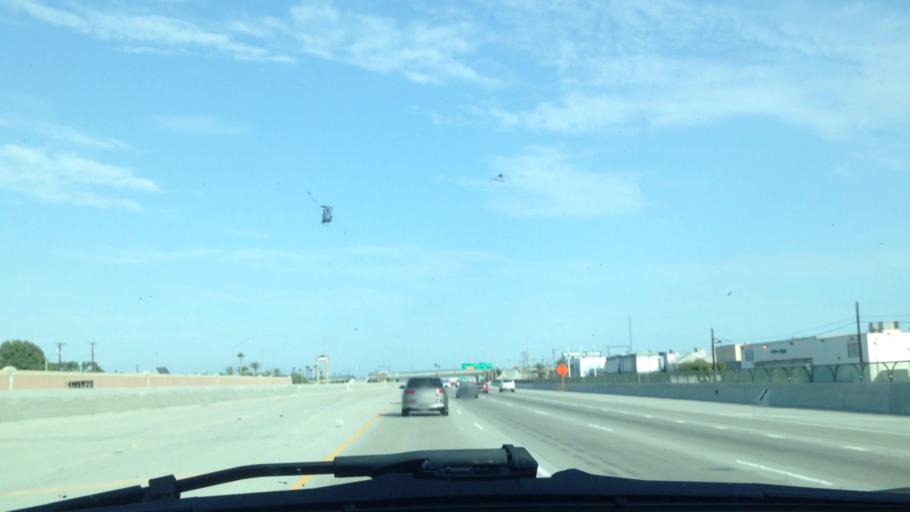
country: US
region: California
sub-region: Los Angeles County
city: Norwalk
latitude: 33.8975
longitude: -118.0537
